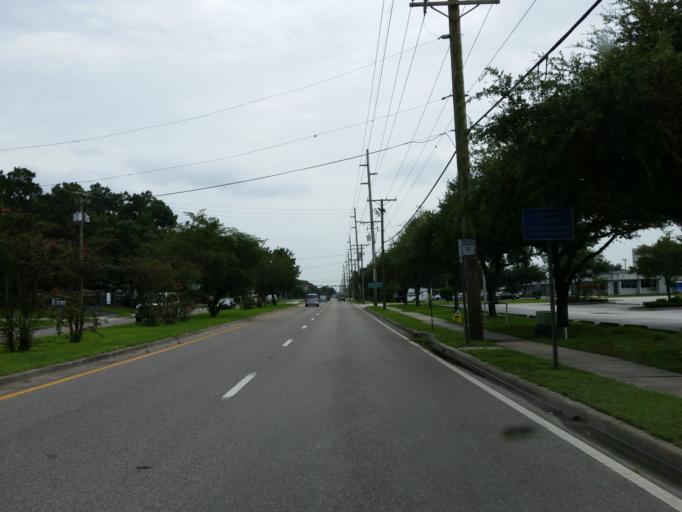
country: US
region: Florida
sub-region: Hillsborough County
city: Mango
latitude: 27.9660
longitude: -82.3353
